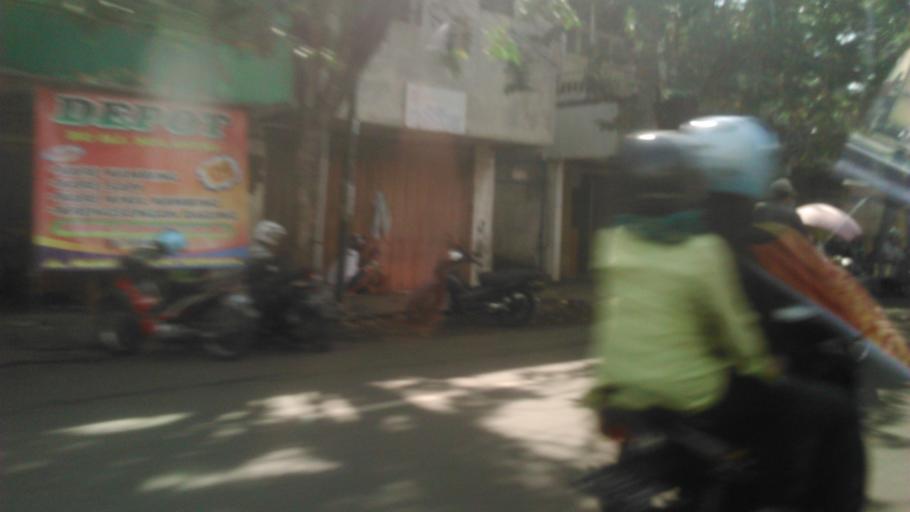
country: ID
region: East Java
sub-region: Kota Surabaya
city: Surabaya
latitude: -7.2491
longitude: 112.7527
